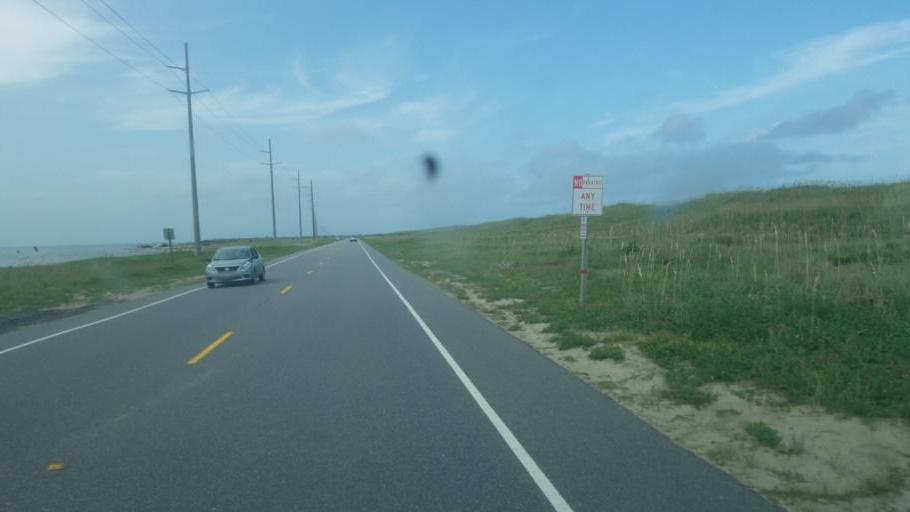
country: US
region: North Carolina
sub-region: Dare County
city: Buxton
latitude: 35.2888
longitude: -75.5155
